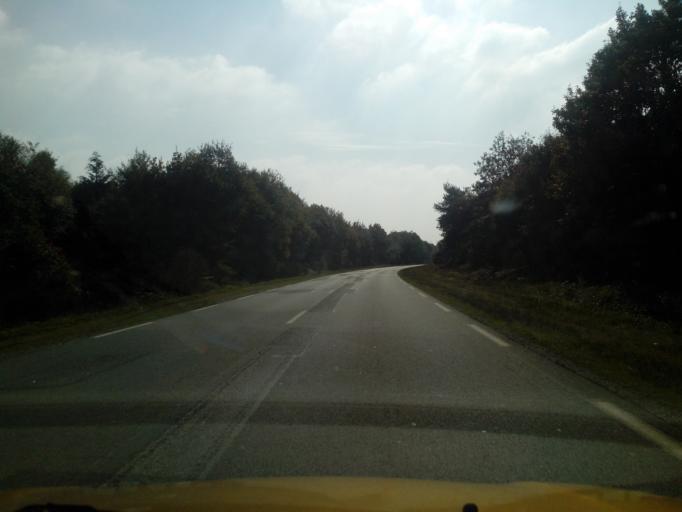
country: FR
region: Brittany
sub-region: Departement du Morbihan
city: Molac
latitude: 47.7501
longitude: -2.4377
